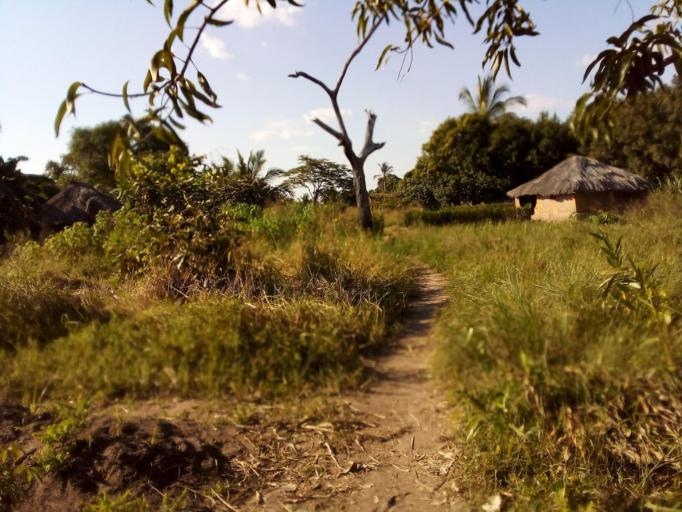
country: MZ
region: Zambezia
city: Quelimane
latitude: -17.5750
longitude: 36.8645
